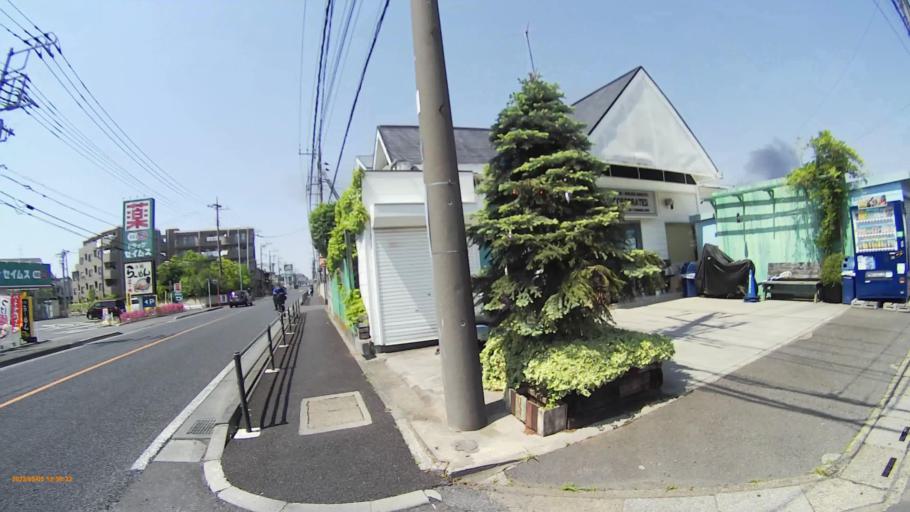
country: JP
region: Saitama
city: Kasukabe
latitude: 35.9580
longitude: 139.7752
